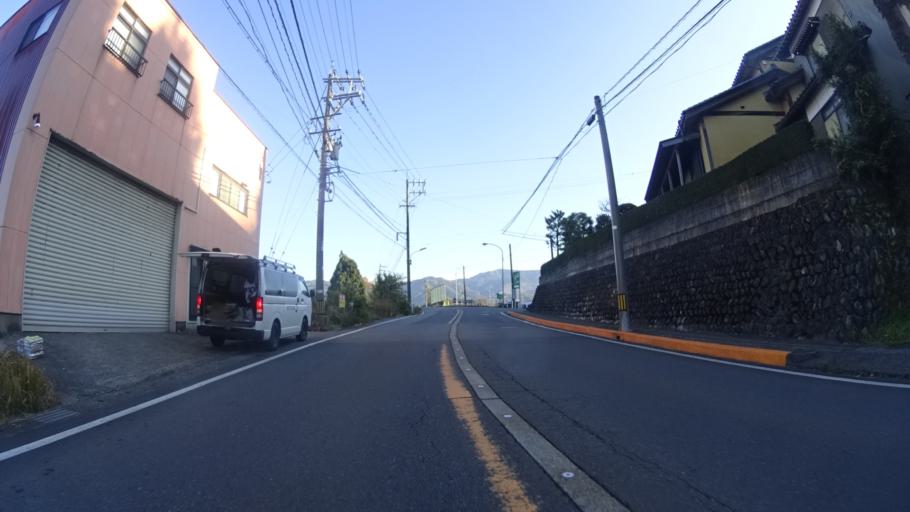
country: JP
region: Fukui
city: Maruoka
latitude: 36.0938
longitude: 136.3028
